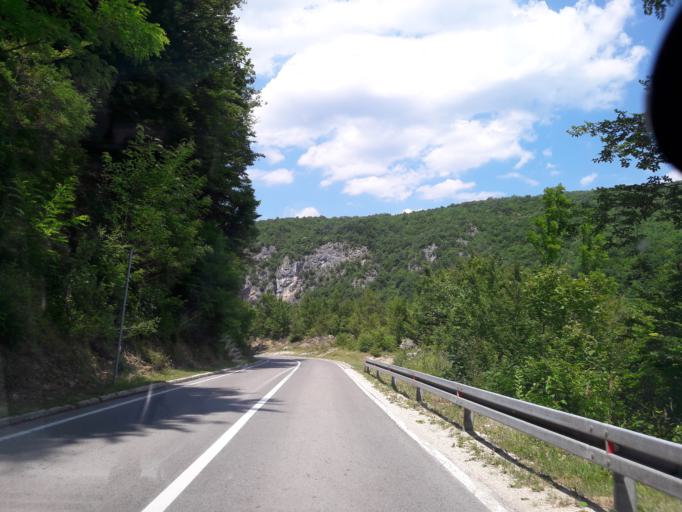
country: BA
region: Republika Srpska
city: Sipovo
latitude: 44.2201
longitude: 17.1191
